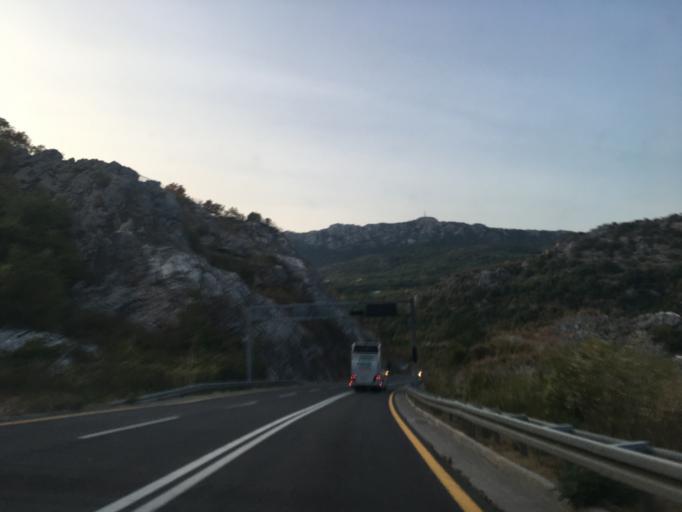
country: ME
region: Bar
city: Sutomore
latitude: 42.2228
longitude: 19.0511
